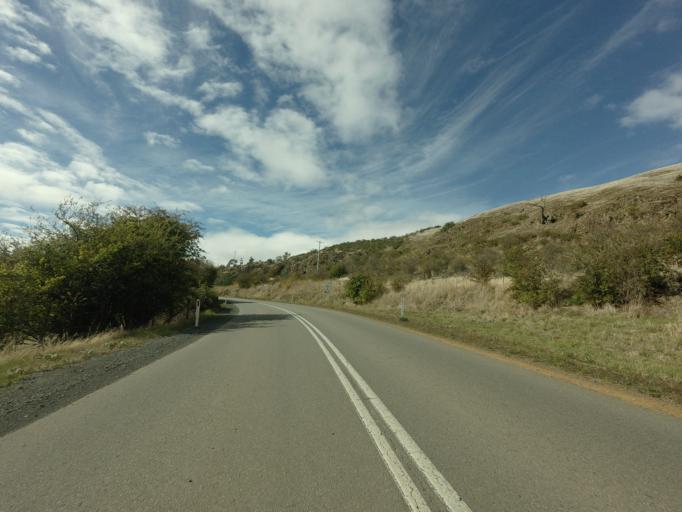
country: AU
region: Tasmania
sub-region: Derwent Valley
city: New Norfolk
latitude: -42.7047
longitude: 146.9149
